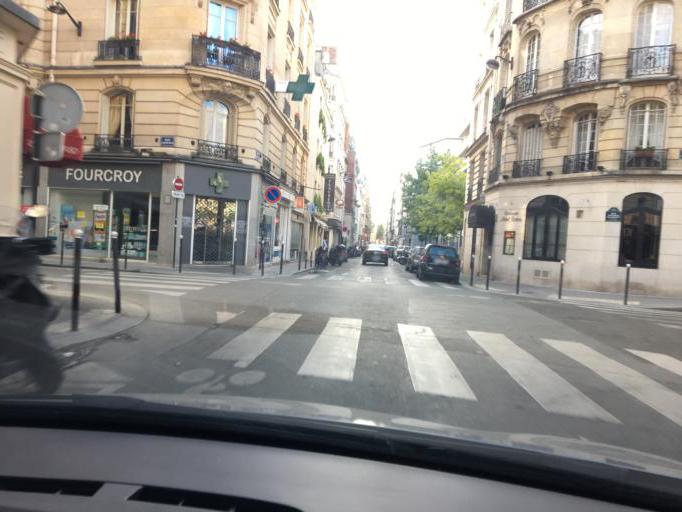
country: FR
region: Ile-de-France
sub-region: Departement des Hauts-de-Seine
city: Levallois-Perret
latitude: 48.8812
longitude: 2.2987
